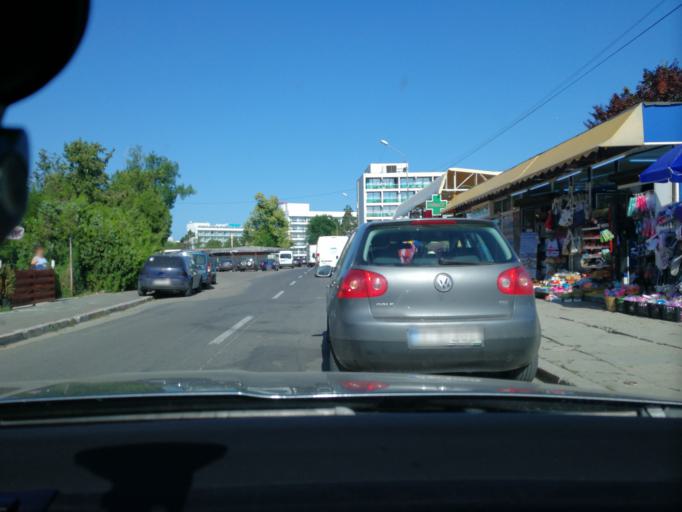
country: RO
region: Constanta
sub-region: Municipiul Mangalia
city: Mangalia
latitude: 43.8438
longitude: 28.5951
